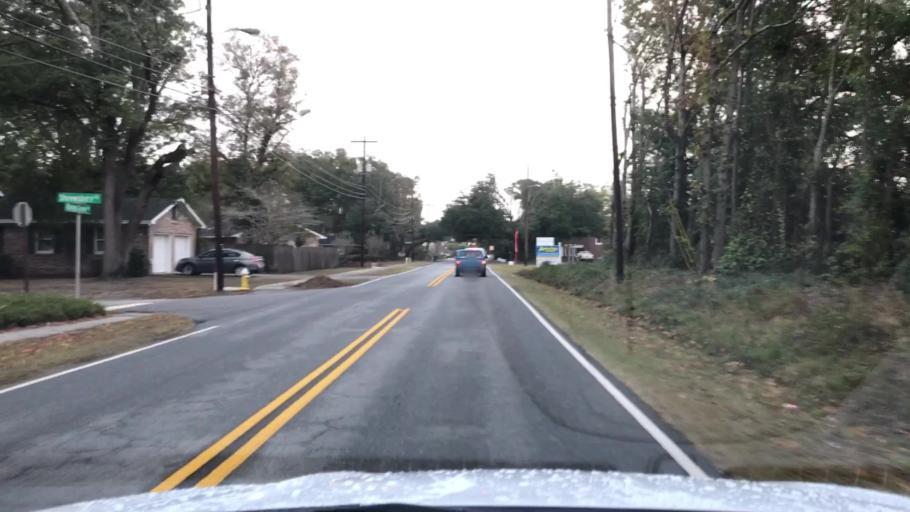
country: US
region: South Carolina
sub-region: Charleston County
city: North Charleston
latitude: 32.8187
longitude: -79.9954
